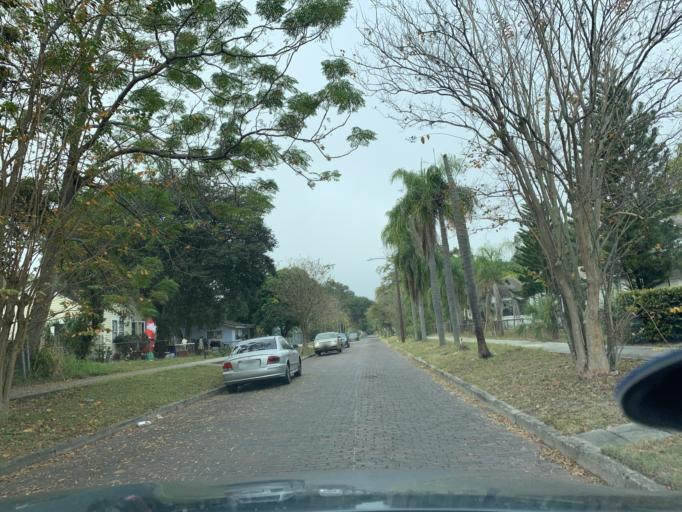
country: US
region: Florida
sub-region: Pinellas County
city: Saint Petersburg
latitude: 27.7553
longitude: -82.6485
